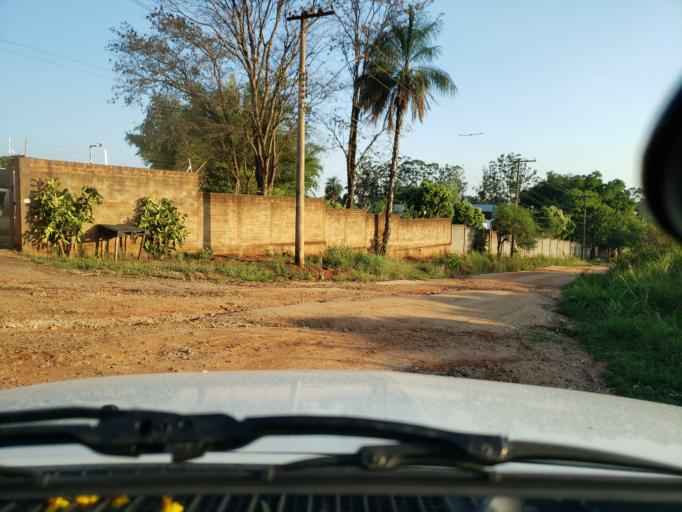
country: BR
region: Sao Paulo
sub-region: Moji-Guacu
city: Mogi-Gaucu
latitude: -22.3373
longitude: -46.9376
